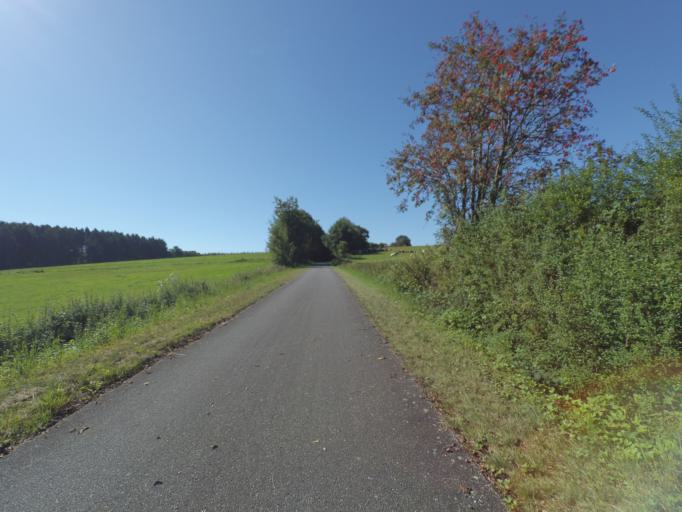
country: DE
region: Rheinland-Pfalz
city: Wallscheid
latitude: 50.1147
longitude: 6.8741
